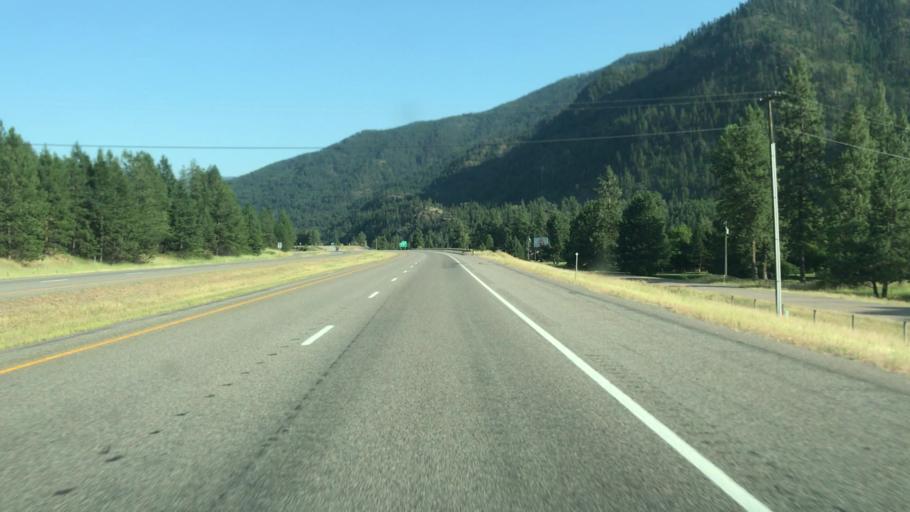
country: US
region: Montana
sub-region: Missoula County
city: Frenchtown
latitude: 47.0119
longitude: -114.5020
